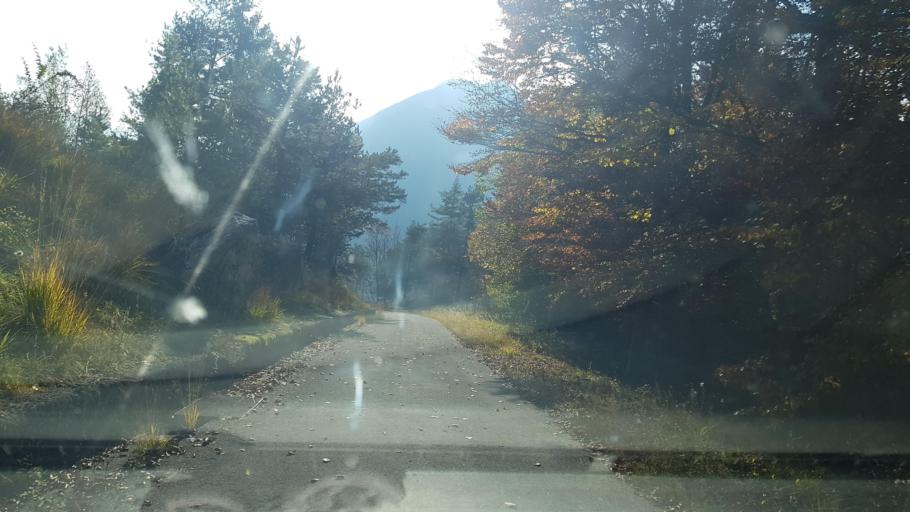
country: IT
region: Friuli Venezia Giulia
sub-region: Provincia di Udine
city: Moggio Udinese
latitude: 46.4507
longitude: 13.2027
